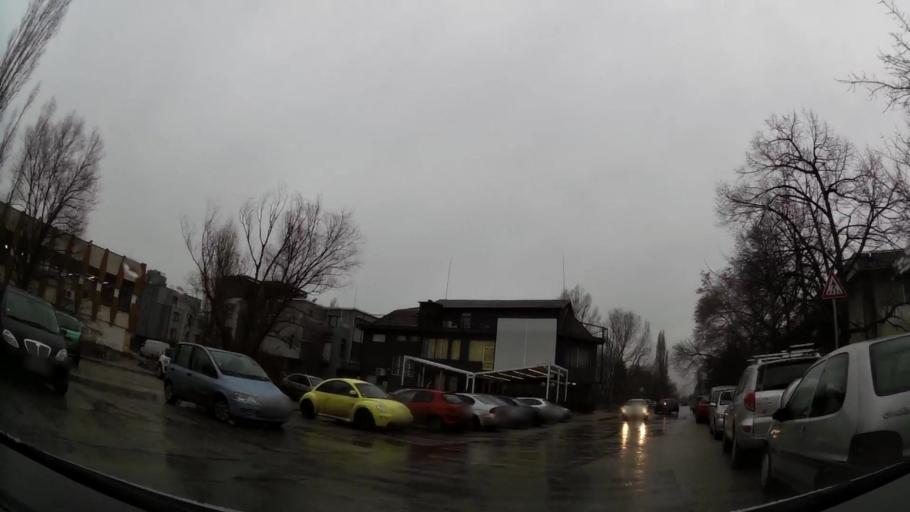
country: BG
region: Sofia-Capital
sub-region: Stolichna Obshtina
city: Sofia
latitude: 42.6575
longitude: 23.3566
